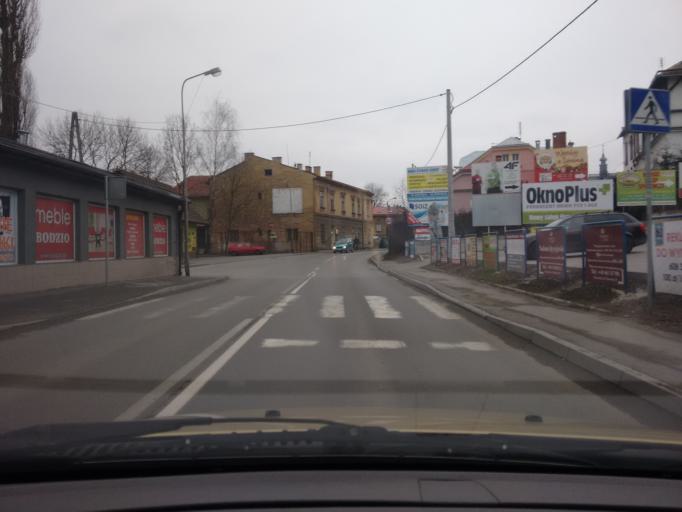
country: PL
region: Silesian Voivodeship
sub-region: Powiat cieszynski
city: Cieszyn
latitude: 49.7528
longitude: 18.6438
